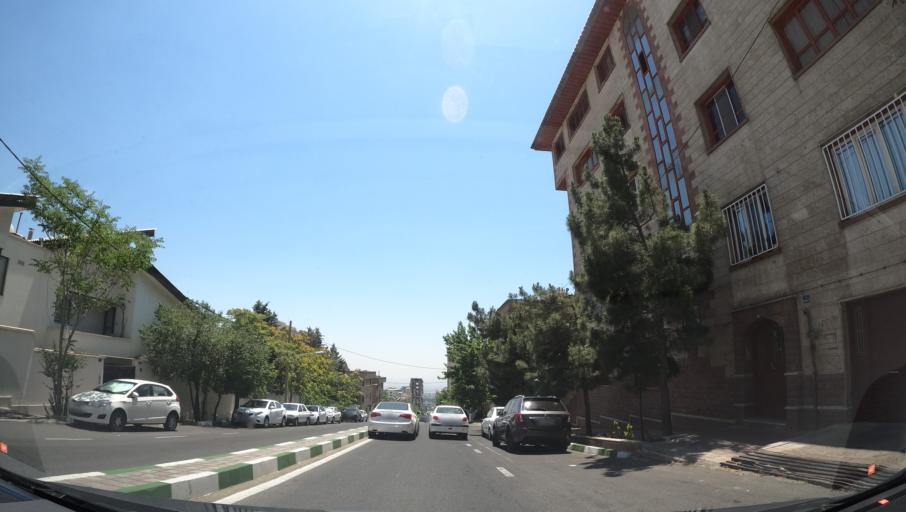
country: IR
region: Tehran
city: Tajrish
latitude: 35.8113
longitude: 51.3994
